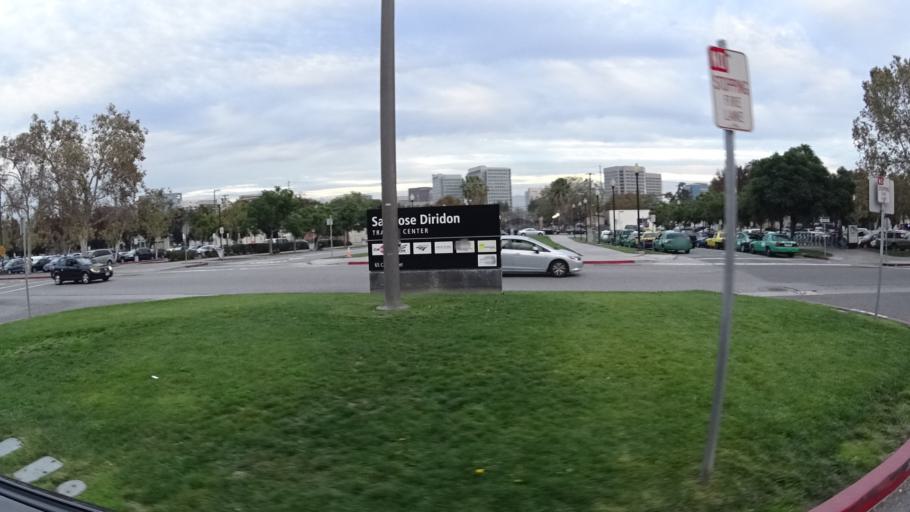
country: US
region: California
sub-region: Santa Clara County
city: San Jose
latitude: 37.3299
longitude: -121.9023
